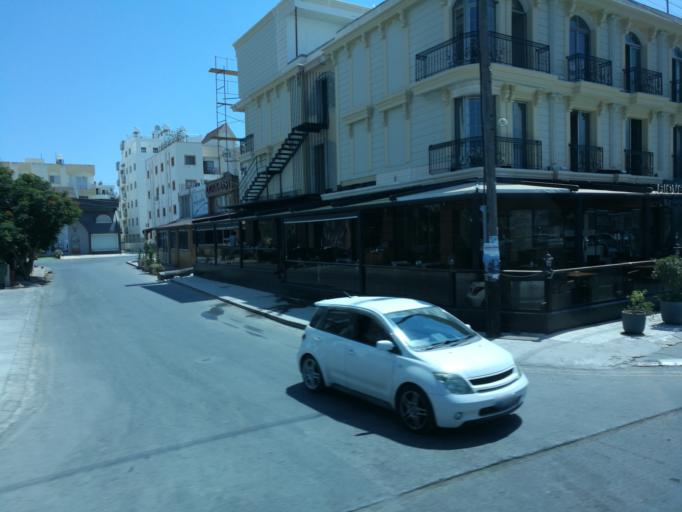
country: CY
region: Ammochostos
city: Famagusta
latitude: 35.1331
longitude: 33.9241
